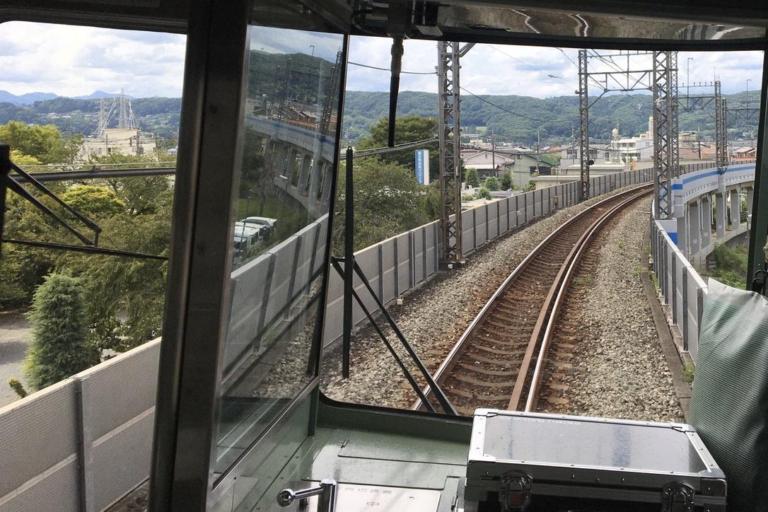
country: JP
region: Saitama
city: Chichibu
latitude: 35.9844
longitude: 139.0833
